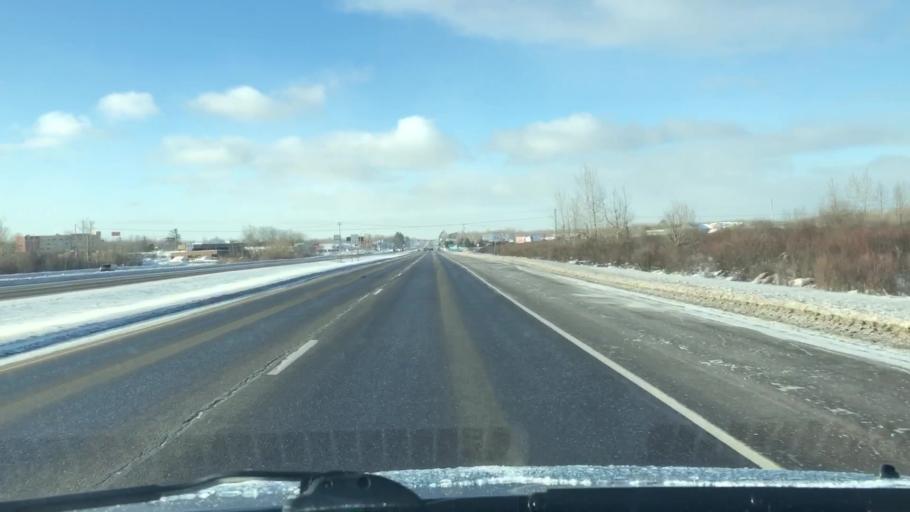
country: US
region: Minnesota
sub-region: Saint Louis County
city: Hermantown
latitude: 46.8119
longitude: -92.1699
